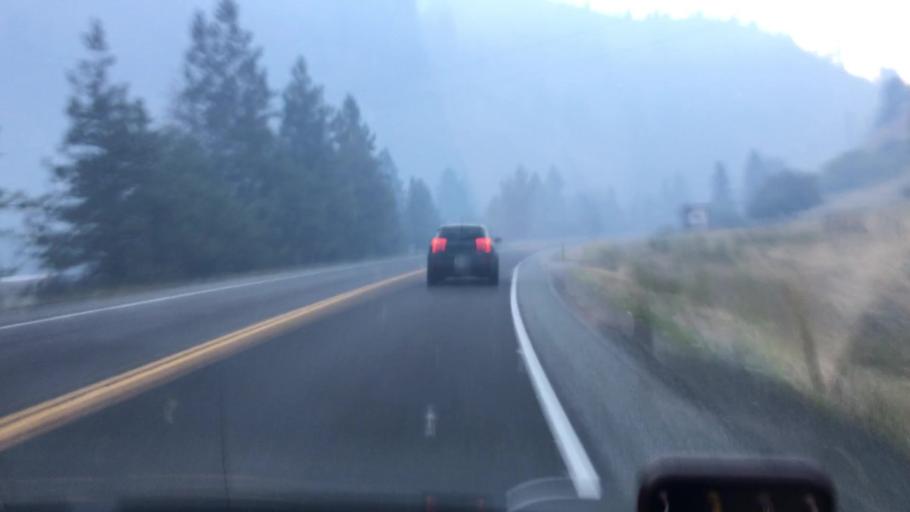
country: US
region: Idaho
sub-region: Valley County
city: McCall
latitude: 45.2702
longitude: -116.3453
